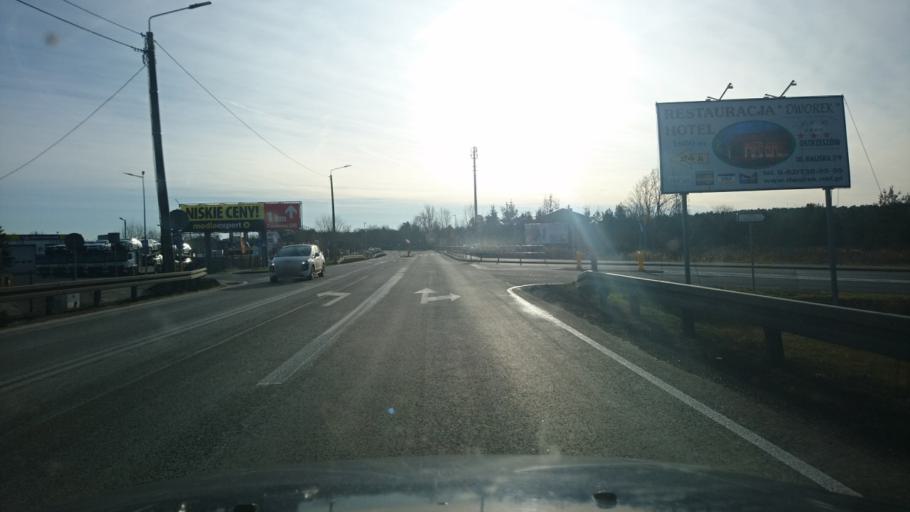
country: PL
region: Greater Poland Voivodeship
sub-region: Powiat ostrzeszowski
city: Ostrzeszow
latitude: 51.4372
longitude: 17.9150
